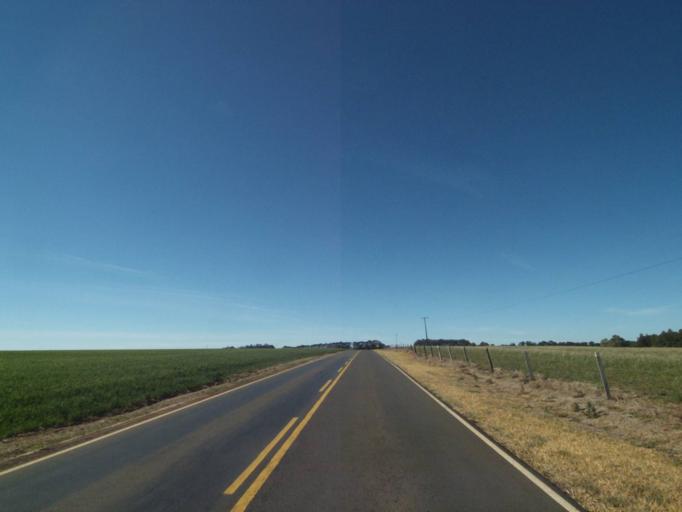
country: BR
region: Parana
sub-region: Tibagi
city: Tibagi
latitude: -24.5445
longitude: -50.3015
